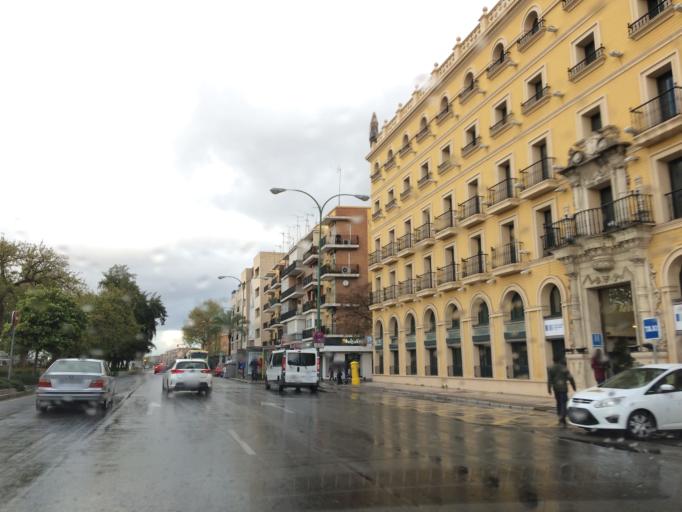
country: ES
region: Andalusia
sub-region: Provincia de Sevilla
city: Sevilla
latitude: 37.4032
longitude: -5.9876
